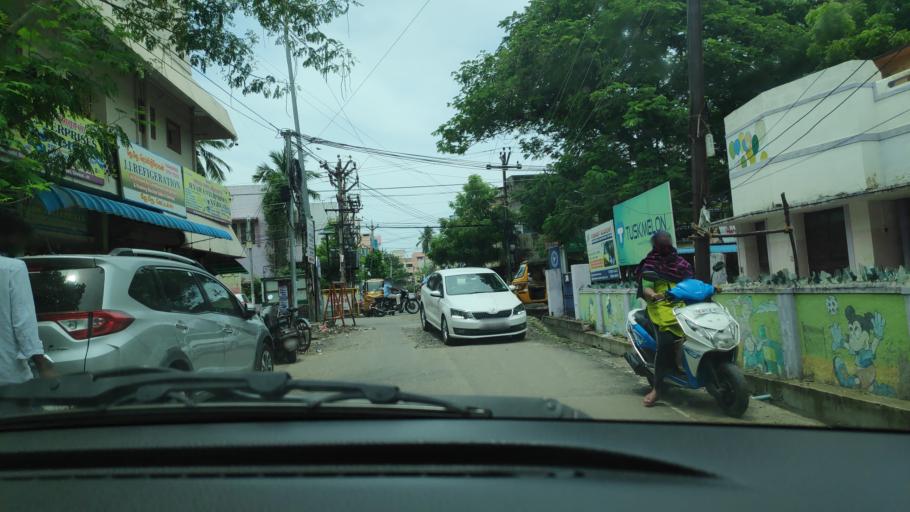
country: IN
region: Tamil Nadu
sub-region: Kancheepuram
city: Pallavaram
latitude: 12.9520
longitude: 80.1445
